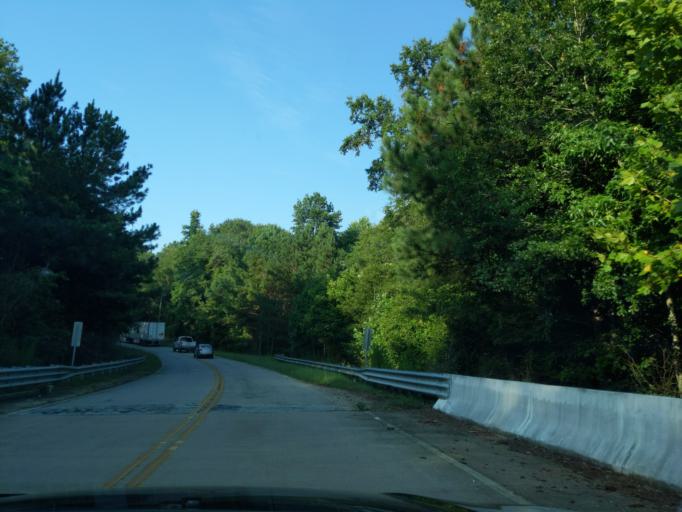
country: US
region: South Carolina
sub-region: Spartanburg County
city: Woodruff
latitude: 34.7827
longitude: -81.9720
